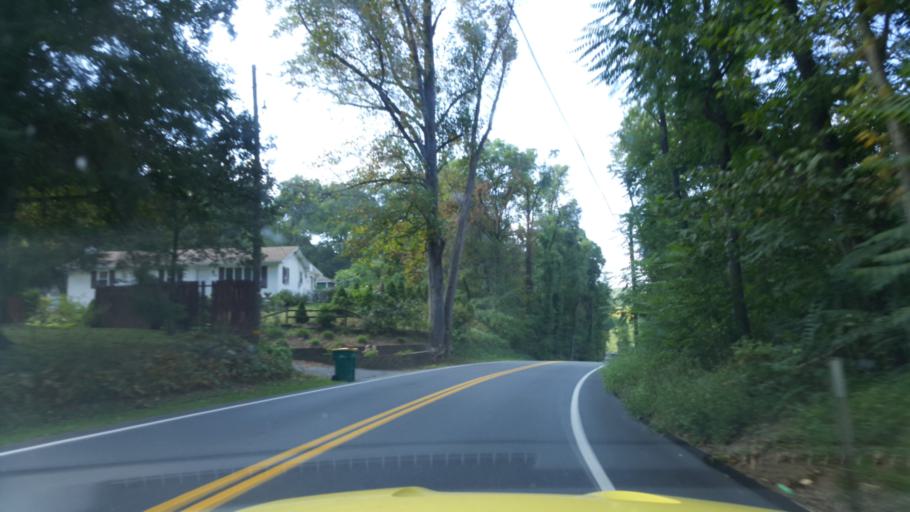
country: US
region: Pennsylvania
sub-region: Lebanon County
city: Campbelltown
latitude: 40.2463
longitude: -76.5378
